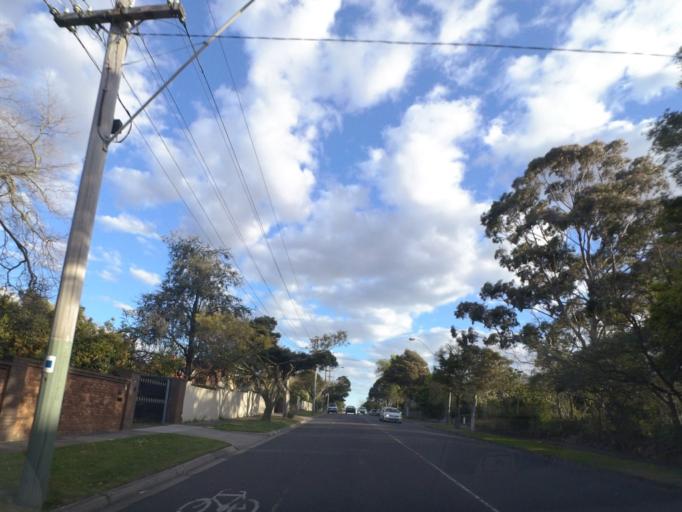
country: AU
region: Victoria
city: Mont Albert
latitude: -37.8128
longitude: 145.0998
